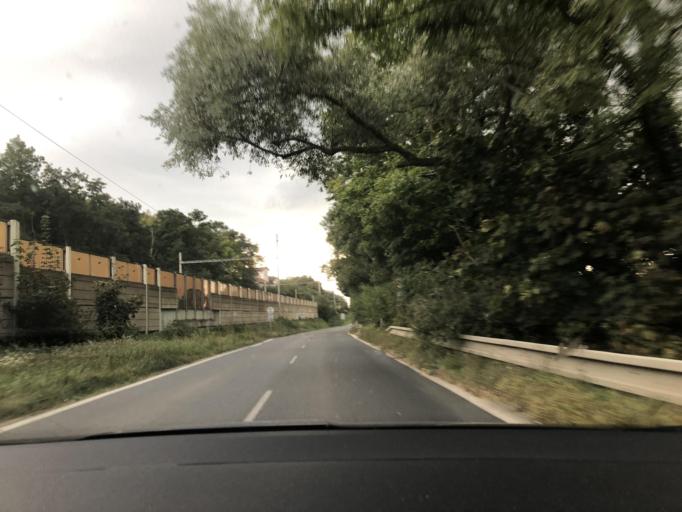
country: CZ
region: Central Bohemia
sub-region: Okres Kolin
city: Tynec nad Labem
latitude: 50.0396
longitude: 15.3627
